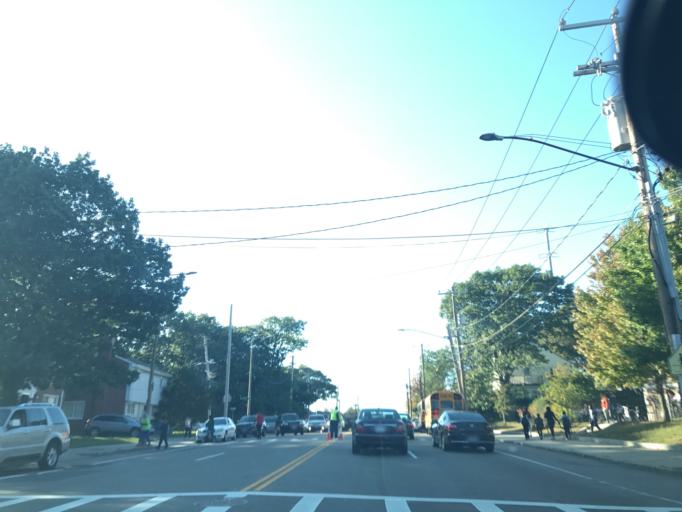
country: US
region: Massachusetts
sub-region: Norfolk County
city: Milton
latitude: 42.2774
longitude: -71.0775
